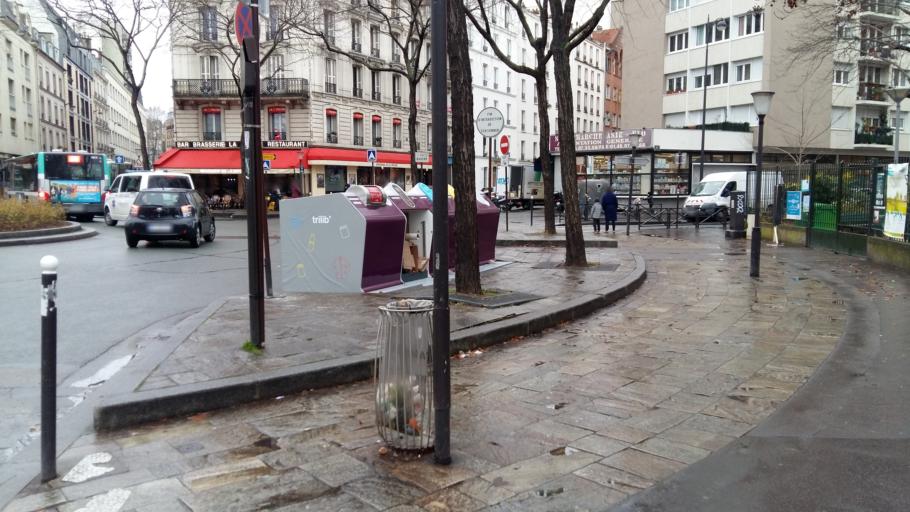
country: FR
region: Ile-de-France
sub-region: Departement de Seine-Saint-Denis
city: Aubervilliers
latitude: 48.8934
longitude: 2.3637
